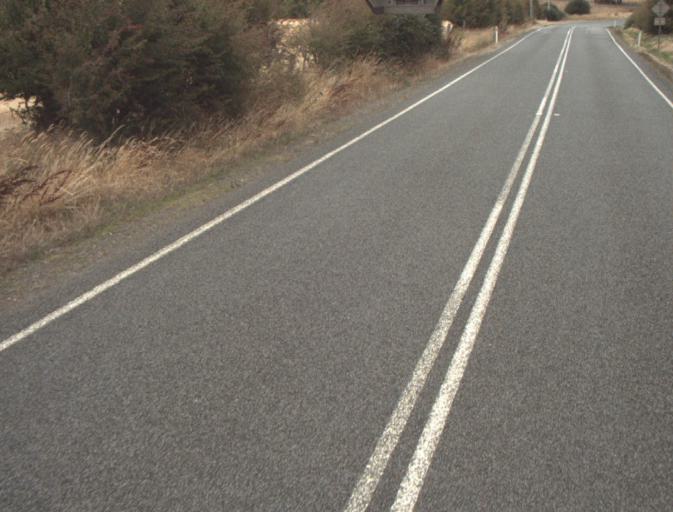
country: AU
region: Tasmania
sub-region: Northern Midlands
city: Evandale
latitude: -41.5045
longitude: 147.2558
